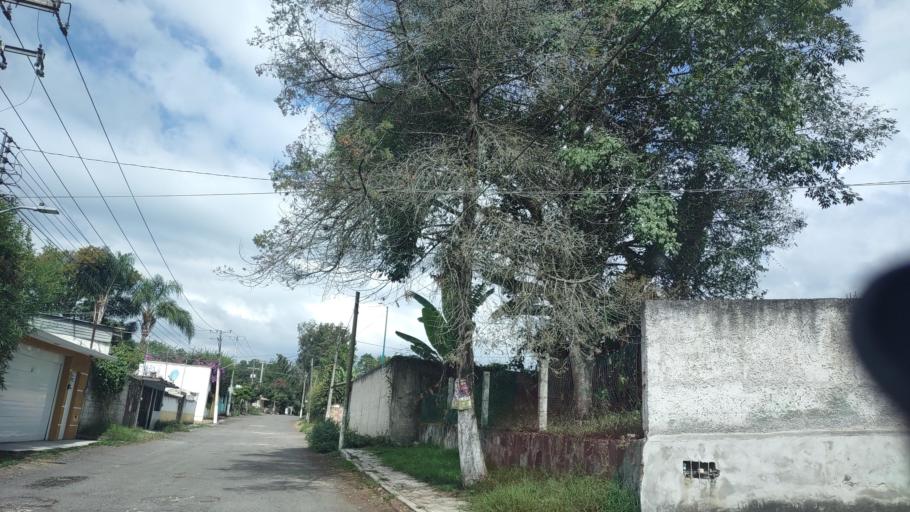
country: MX
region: Veracruz
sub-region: Xalapa
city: Xalapa de Enriquez
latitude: 19.5085
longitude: -96.9380
